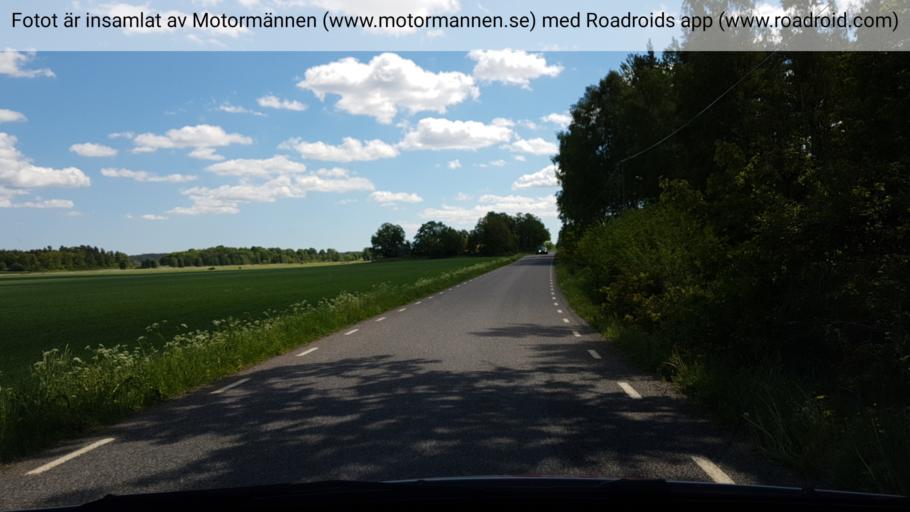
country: SE
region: Kalmar
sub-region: Vasterviks Kommun
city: Forserum
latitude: 57.9979
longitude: 16.5958
